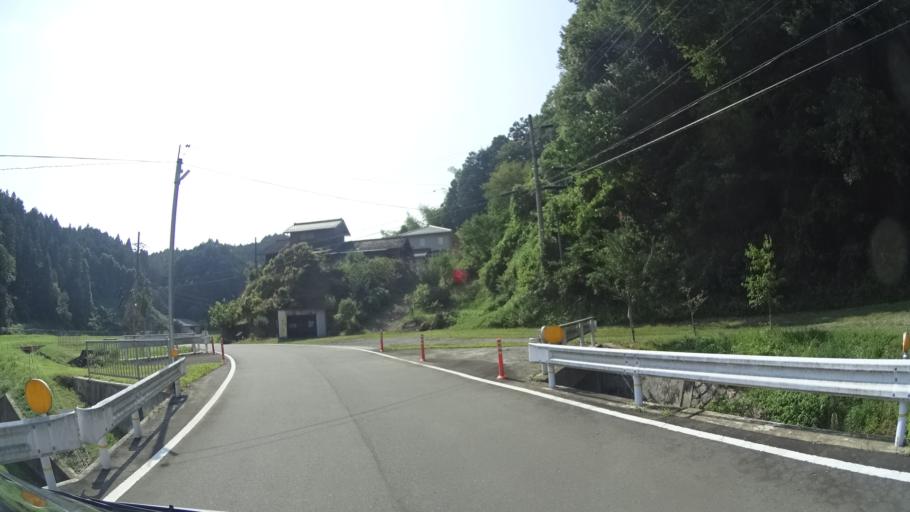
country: JP
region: Kyoto
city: Ayabe
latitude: 35.4027
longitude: 135.2045
